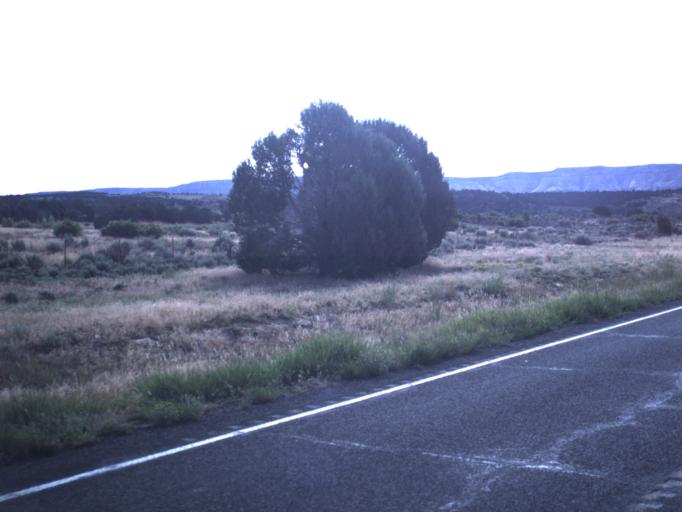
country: US
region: Utah
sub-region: Kane County
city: Kanab
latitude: 37.2377
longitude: -112.7461
